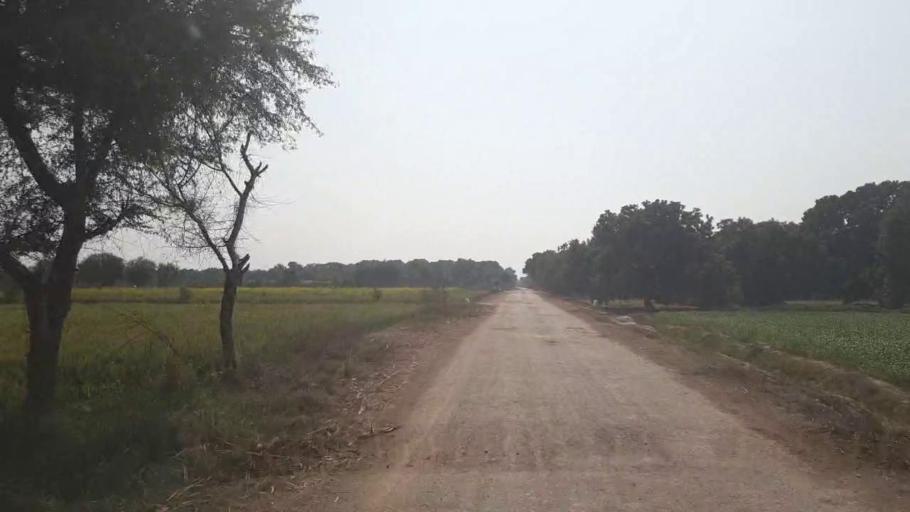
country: PK
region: Sindh
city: Tando Allahyar
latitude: 25.4792
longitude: 68.8260
